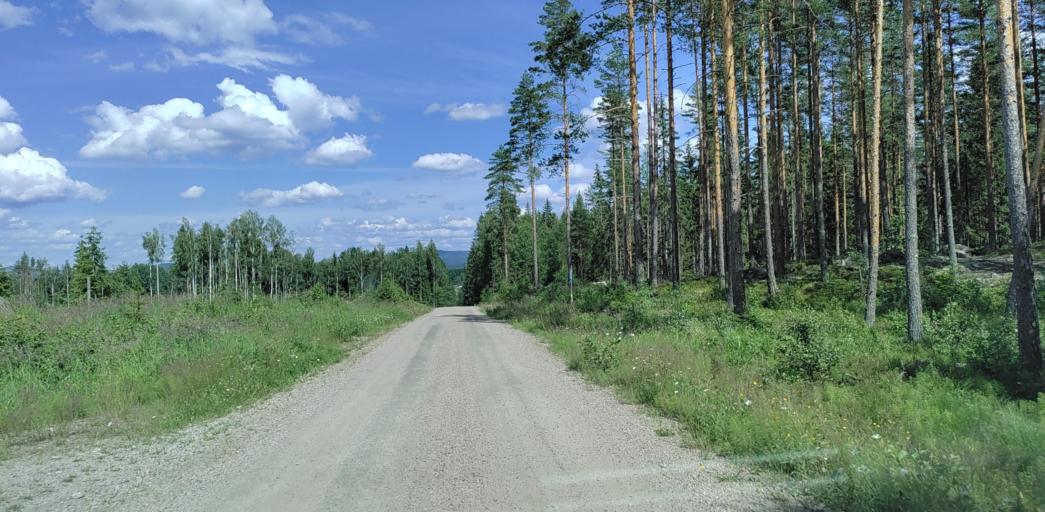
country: SE
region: Vaermland
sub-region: Hagfors Kommun
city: Ekshaerad
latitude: 60.0982
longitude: 13.4385
